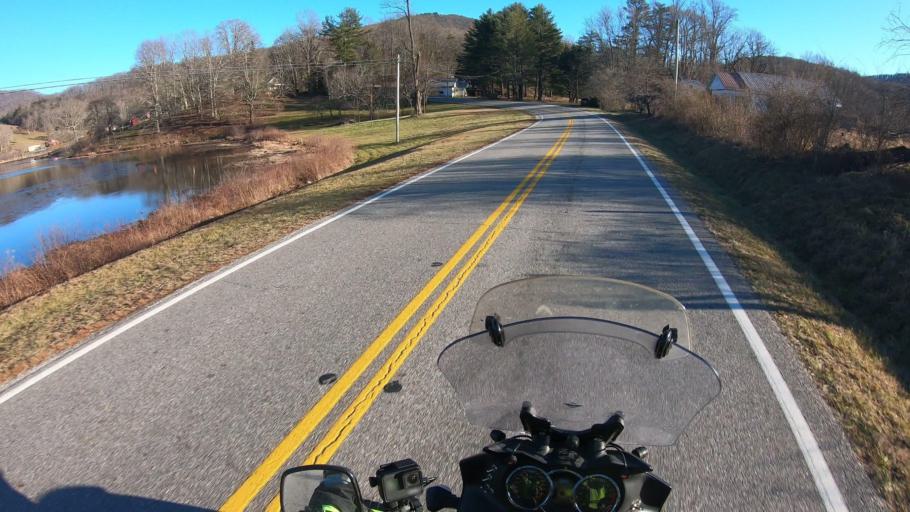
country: US
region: Georgia
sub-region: Lumpkin County
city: Dahlonega
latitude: 34.6951
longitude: -84.0236
